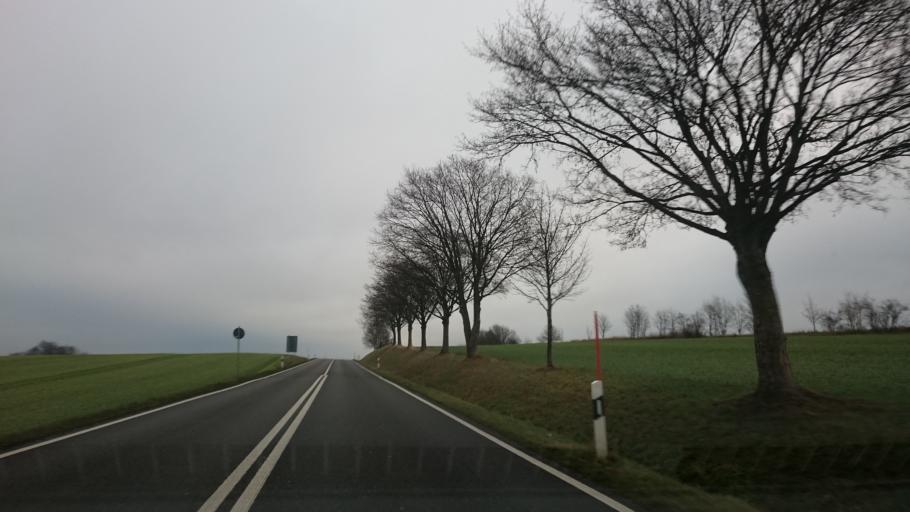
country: DE
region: Saxony
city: Mulsen
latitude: 50.7414
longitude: 12.5839
